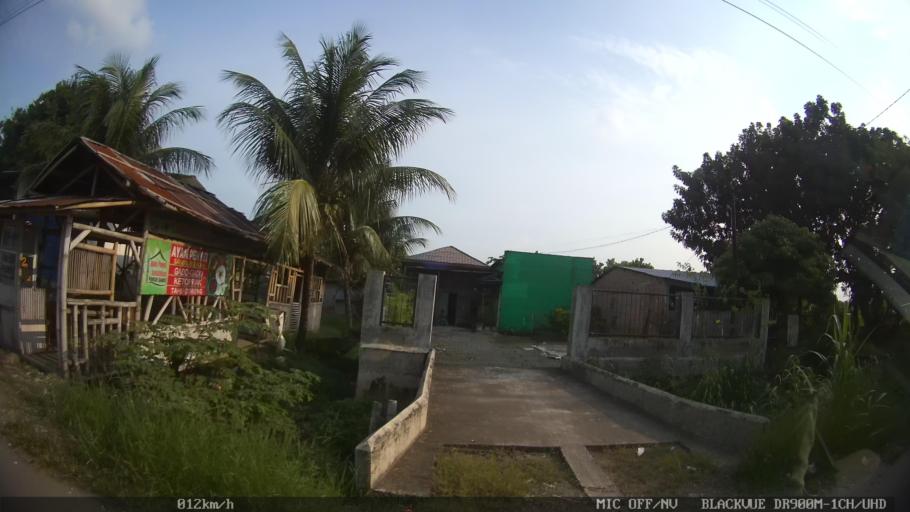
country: ID
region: North Sumatra
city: Medan
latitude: 3.5813
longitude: 98.7542
